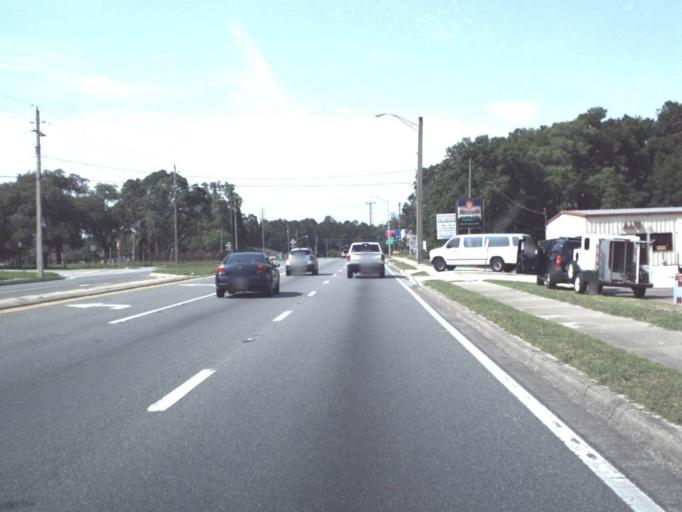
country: US
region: Florida
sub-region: Clay County
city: Middleburg
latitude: 30.0716
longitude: -81.8653
